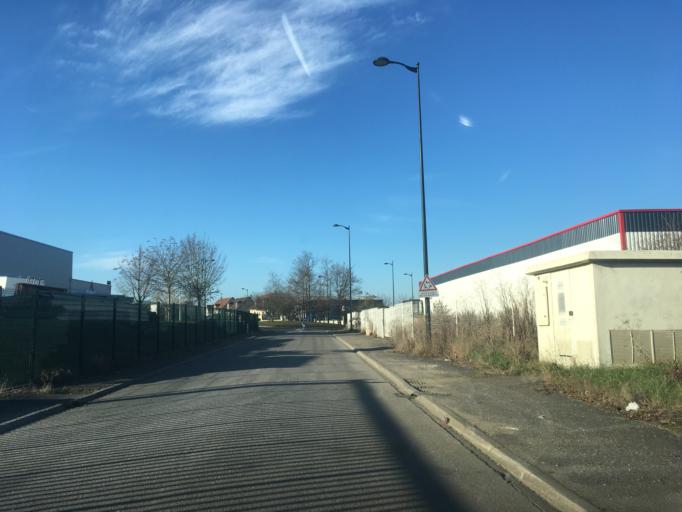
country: FR
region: Haute-Normandie
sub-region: Departement de l'Eure
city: Vernon
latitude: 49.0792
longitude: 1.5015
